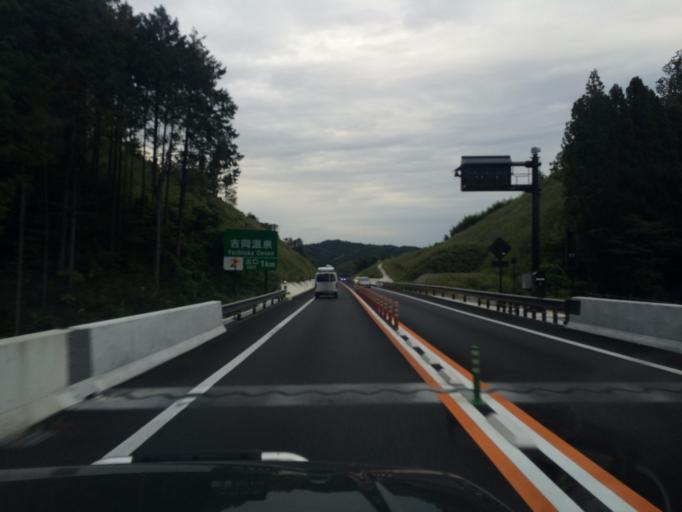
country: JP
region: Tottori
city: Tottori
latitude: 35.4983
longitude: 134.1204
